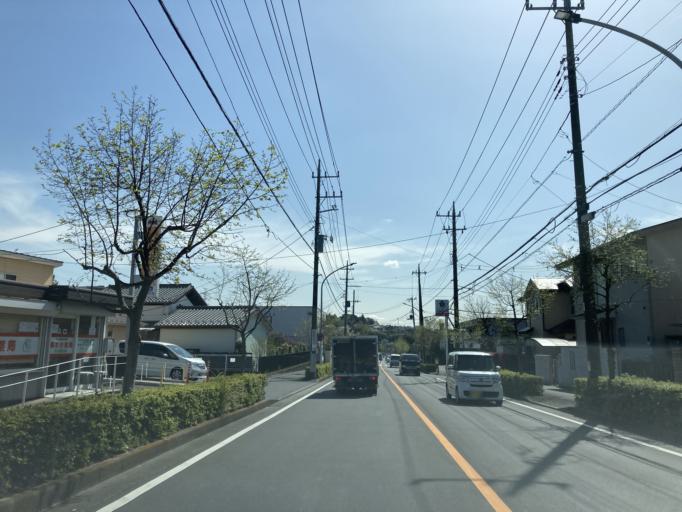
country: JP
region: Tokyo
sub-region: Machida-shi
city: Machida
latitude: 35.6051
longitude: 139.4763
